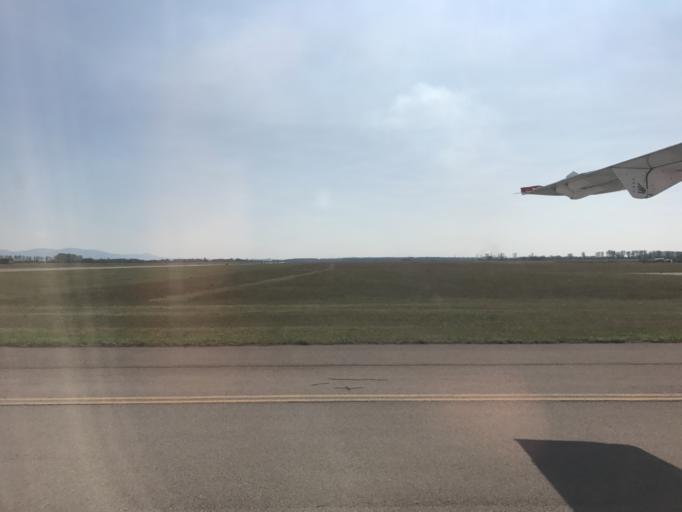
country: SK
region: Kosicky
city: Kosice
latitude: 48.6719
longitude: 21.2415
